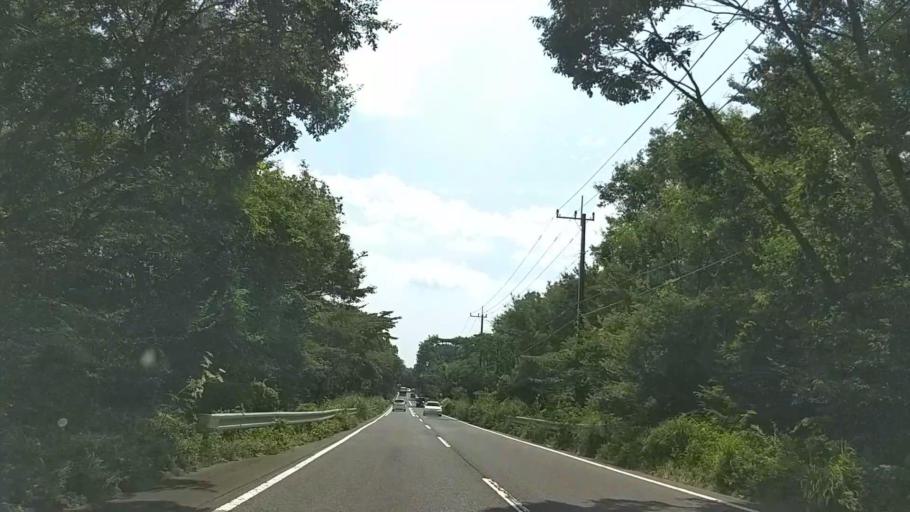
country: JP
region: Shizuoka
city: Fujinomiya
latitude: 35.3630
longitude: 138.5775
